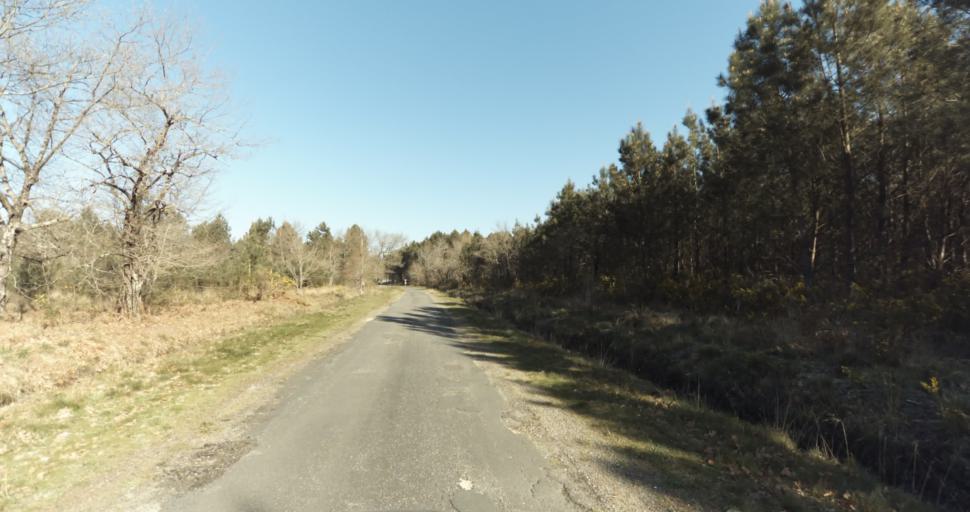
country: FR
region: Aquitaine
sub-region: Departement de la Gironde
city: Martignas-sur-Jalle
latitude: 44.8121
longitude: -0.8540
